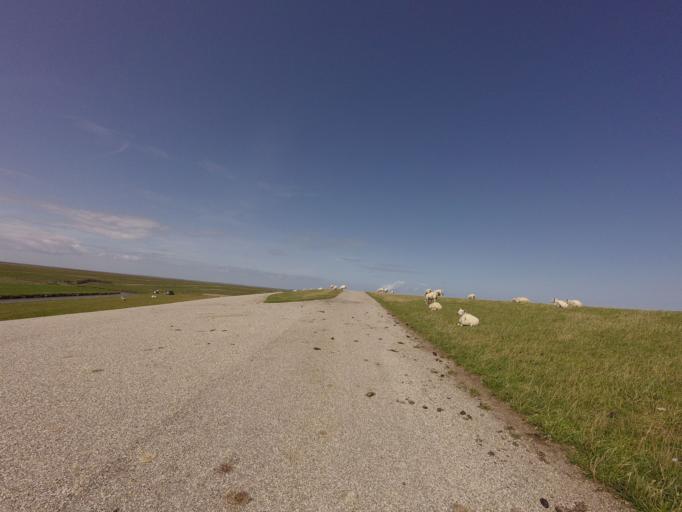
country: NL
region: Friesland
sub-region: Gemeente Dongeradeel
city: Holwerd
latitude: 53.3690
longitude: 5.8590
